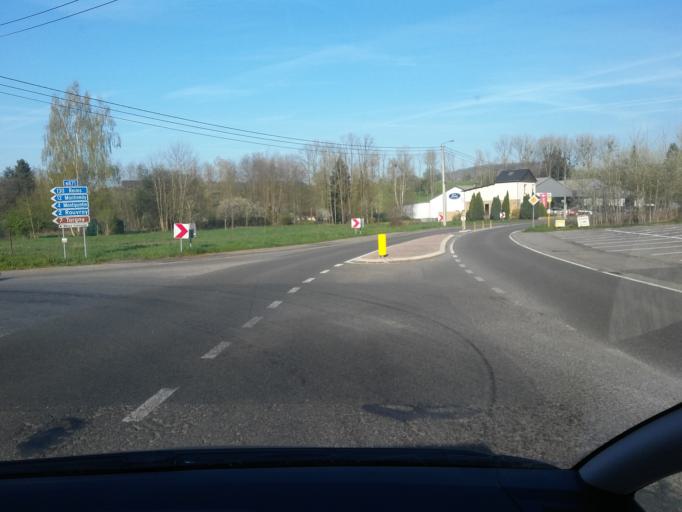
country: BE
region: Wallonia
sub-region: Province du Luxembourg
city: Rouvroy
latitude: 49.5590
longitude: 5.4997
